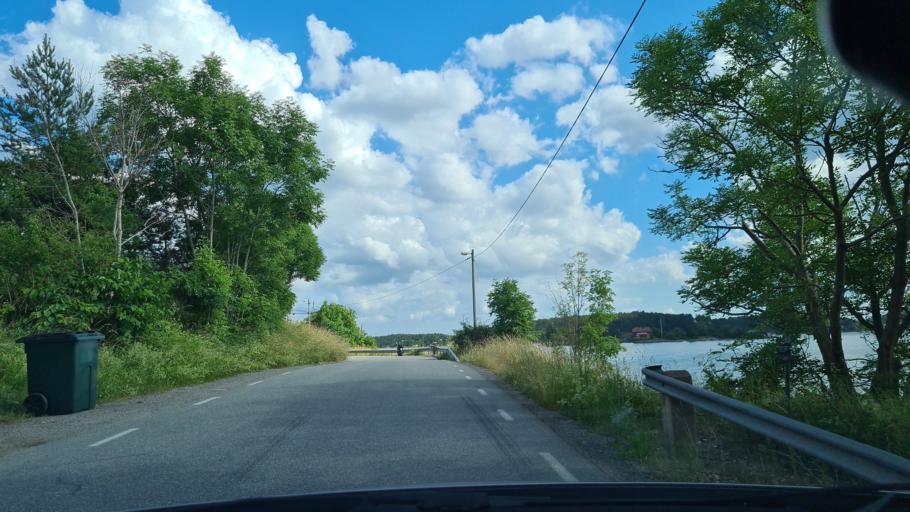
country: SE
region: Stockholm
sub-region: Vaxholms Kommun
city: Vaxholm
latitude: 59.4044
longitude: 18.3633
